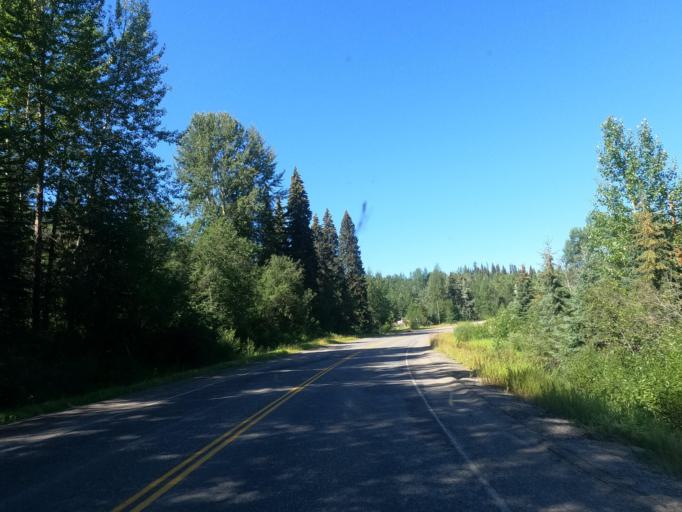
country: CA
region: British Columbia
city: Quesnel
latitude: 53.0509
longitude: -122.1838
